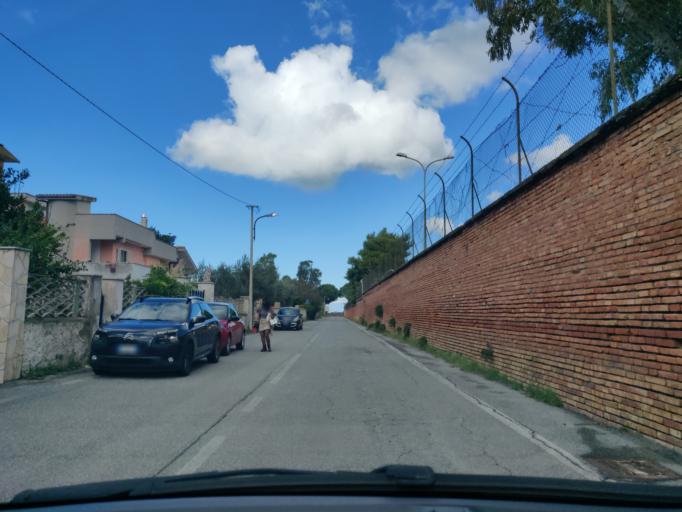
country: IT
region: Latium
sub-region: Citta metropolitana di Roma Capitale
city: Aurelia
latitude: 42.1389
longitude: 11.7875
